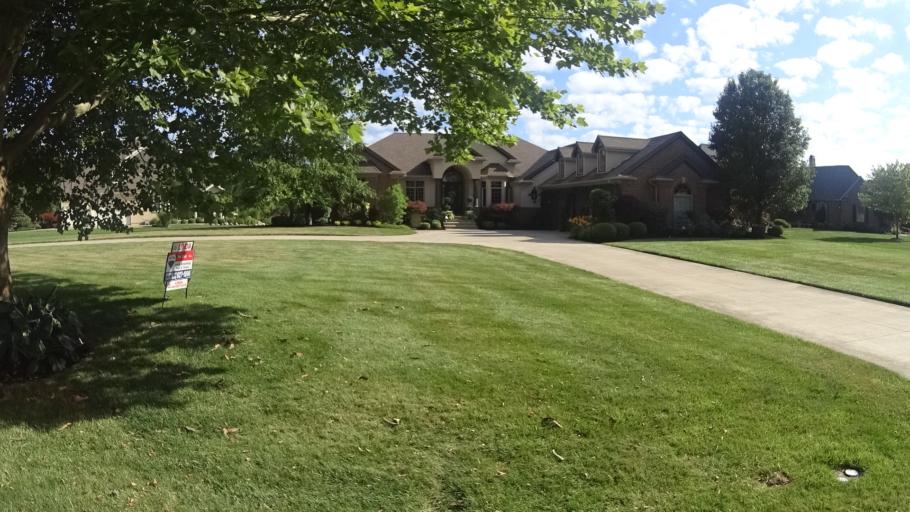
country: US
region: Ohio
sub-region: Erie County
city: Sandusky
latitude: 41.4148
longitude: -82.6574
